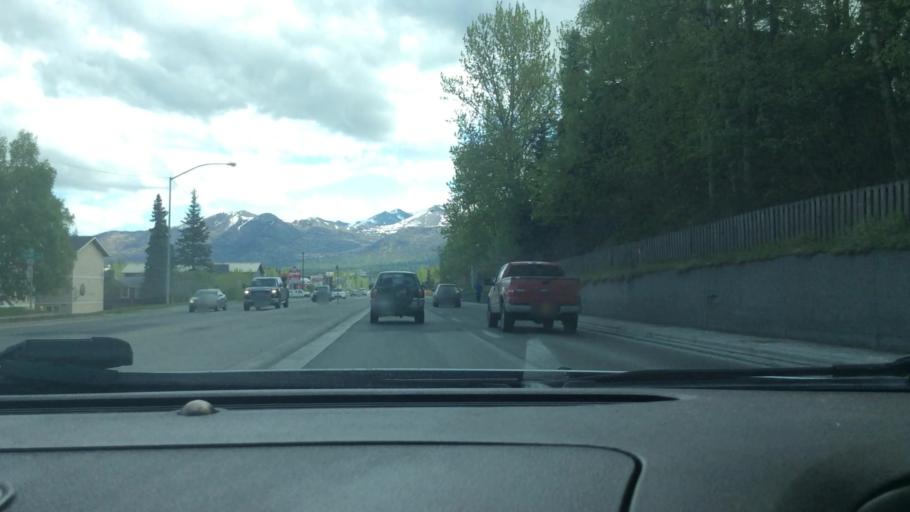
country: US
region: Alaska
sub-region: Anchorage Municipality
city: Anchorage
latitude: 61.1808
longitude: -149.8217
